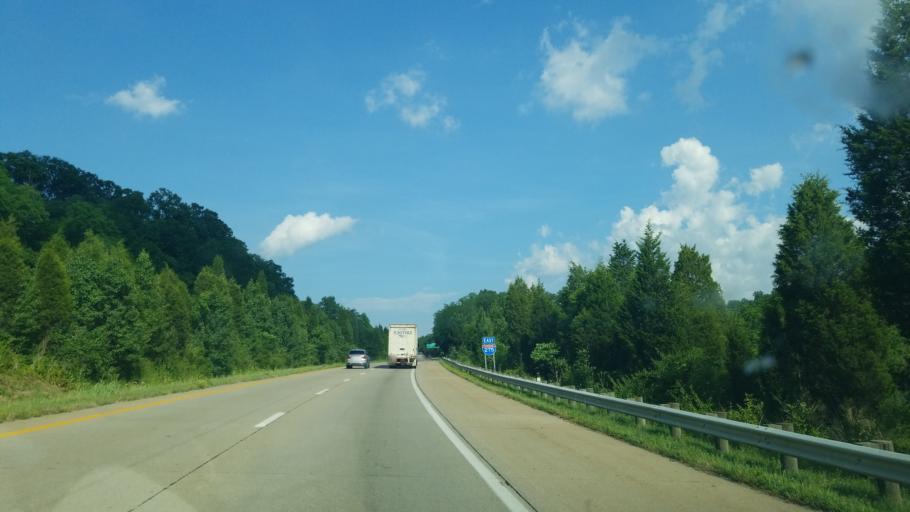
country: US
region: Ohio
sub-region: Hamilton County
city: Salem Heights
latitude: 39.0574
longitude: -84.3823
